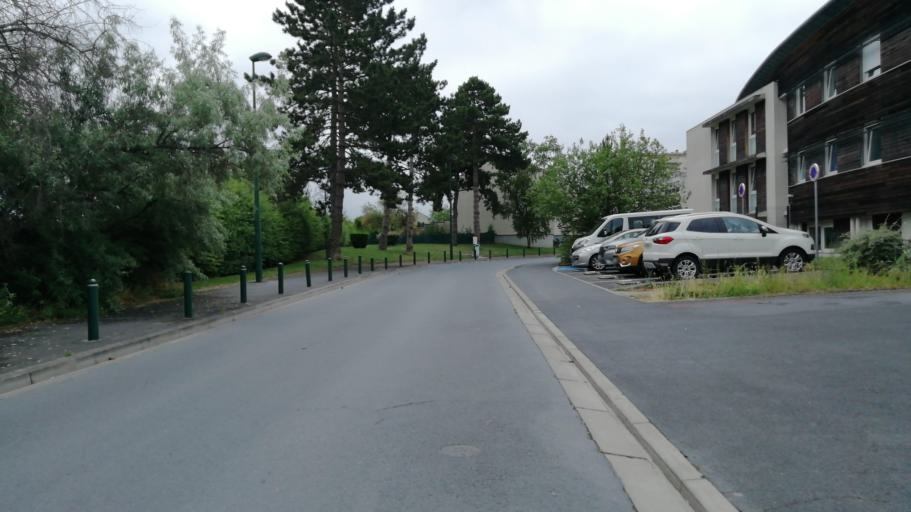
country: FR
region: Champagne-Ardenne
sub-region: Departement de la Marne
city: Betheny
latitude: 49.2542
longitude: 4.0659
